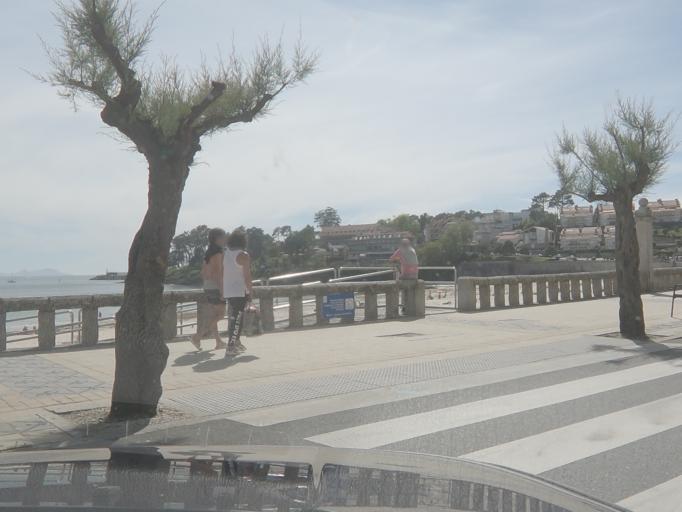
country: ES
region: Galicia
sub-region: Provincia de Pontevedra
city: Sanxenxo
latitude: 42.4016
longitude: -8.8129
